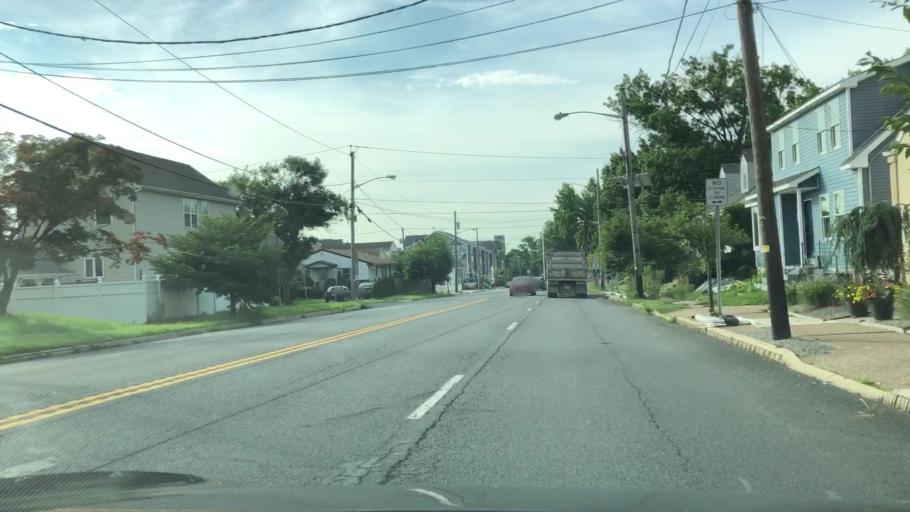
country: US
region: New Jersey
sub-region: Mercer County
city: Prospect Park
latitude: 40.2442
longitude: -74.7416
